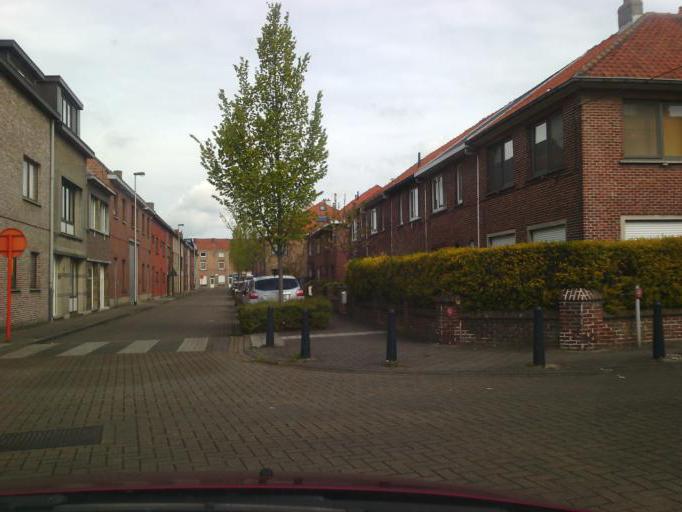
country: BE
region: Flanders
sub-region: Provincie Oost-Vlaanderen
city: Gent
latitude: 51.0664
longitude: 3.6915
